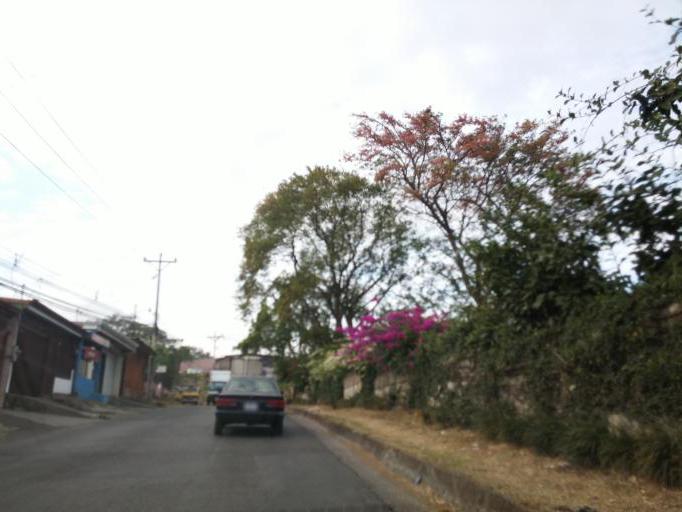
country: CR
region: Alajuela
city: Alajuela
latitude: 9.9791
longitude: -84.2254
